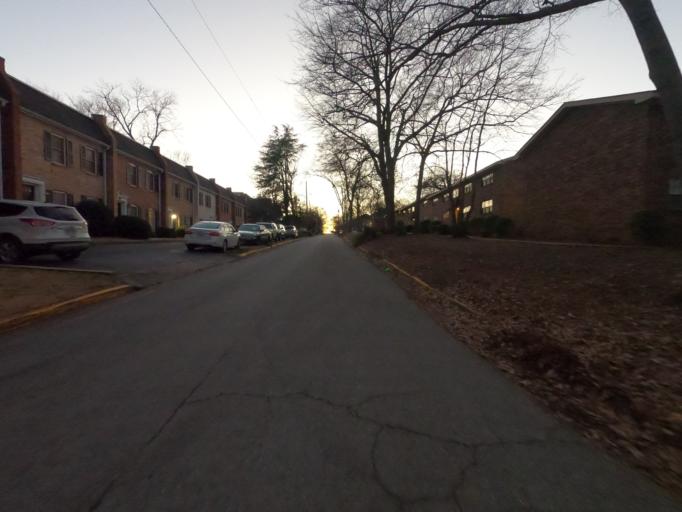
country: US
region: Georgia
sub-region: Clarke County
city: Athens
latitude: 33.9533
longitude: -83.3849
